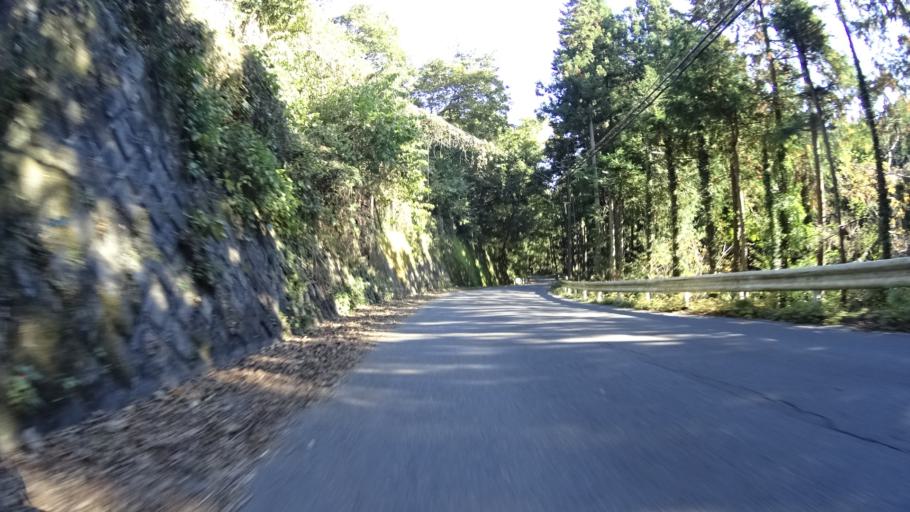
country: JP
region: Yamanashi
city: Uenohara
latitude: 35.6391
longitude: 139.1365
